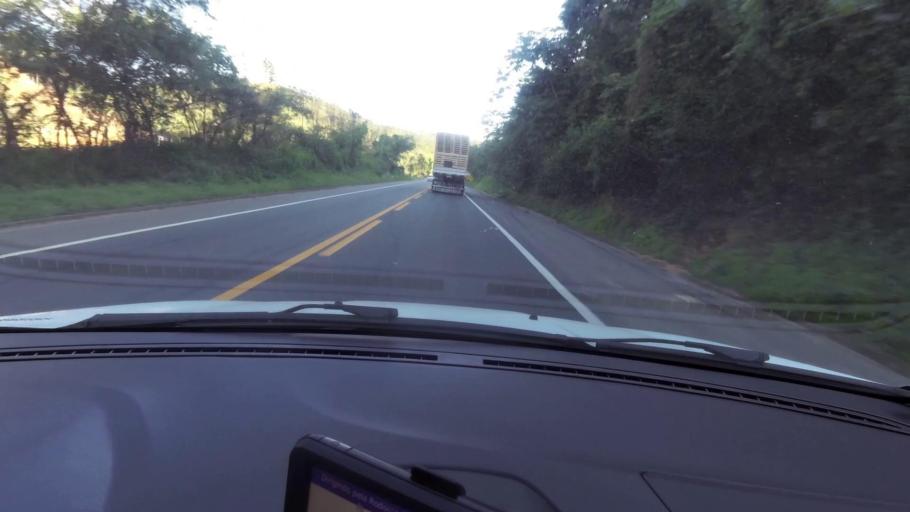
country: BR
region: Espirito Santo
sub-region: Alfredo Chaves
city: Alfredo Chaves
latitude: -20.6616
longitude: -40.6513
